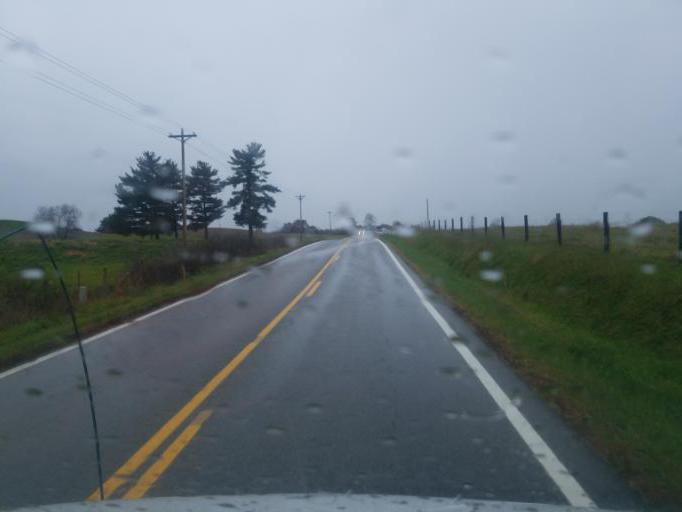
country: US
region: Ohio
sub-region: Washington County
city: Beverly
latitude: 39.4664
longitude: -81.6529
